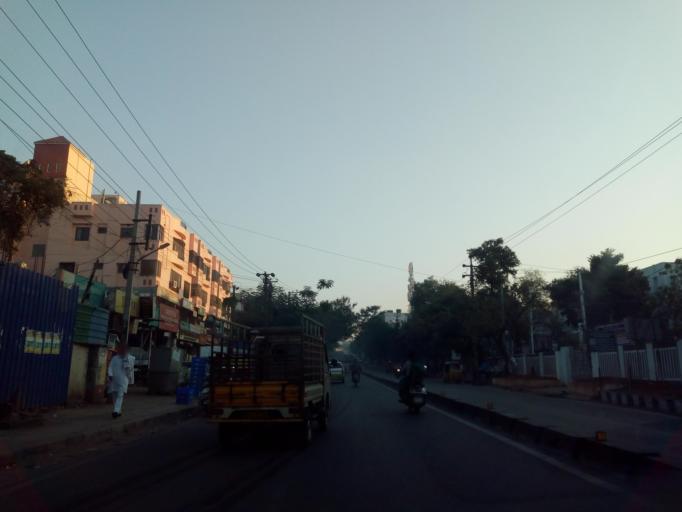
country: IN
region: Telangana
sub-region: Rangareddi
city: Gaddi Annaram
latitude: 17.4021
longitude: 78.5096
